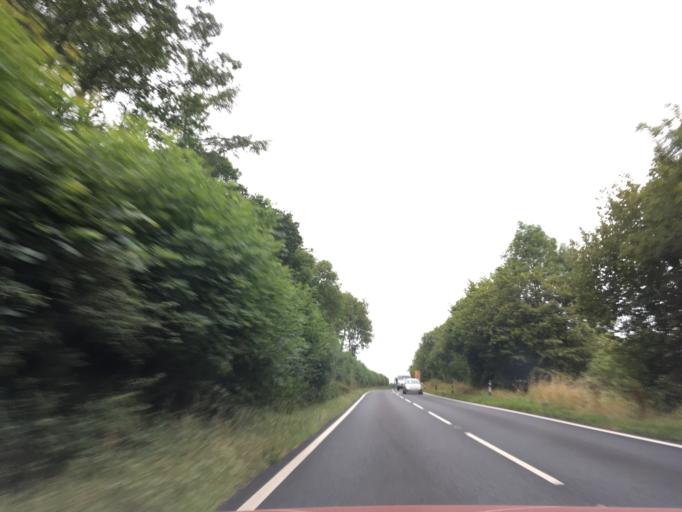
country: GB
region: Wales
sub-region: Blaenau Gwent
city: Brynmawr
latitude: 51.8846
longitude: -3.2009
